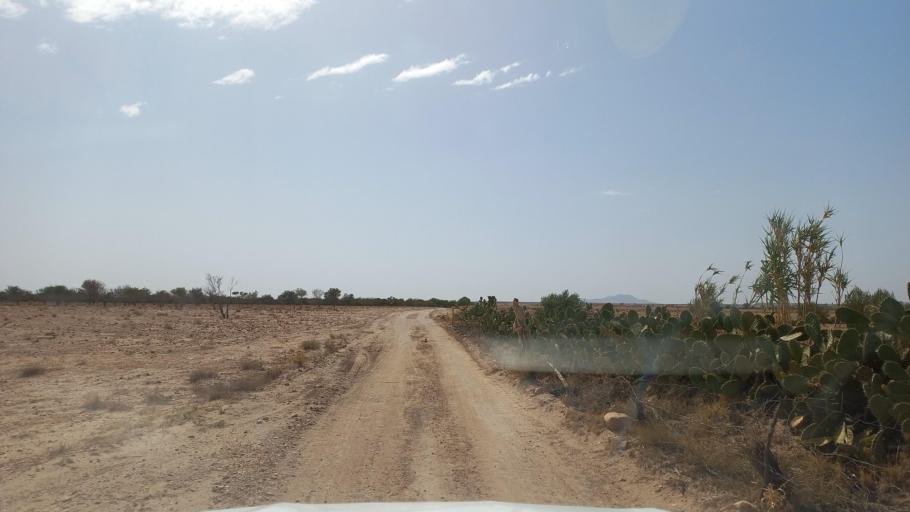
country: TN
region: Al Qasrayn
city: Kasserine
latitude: 35.2579
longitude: 8.9690
